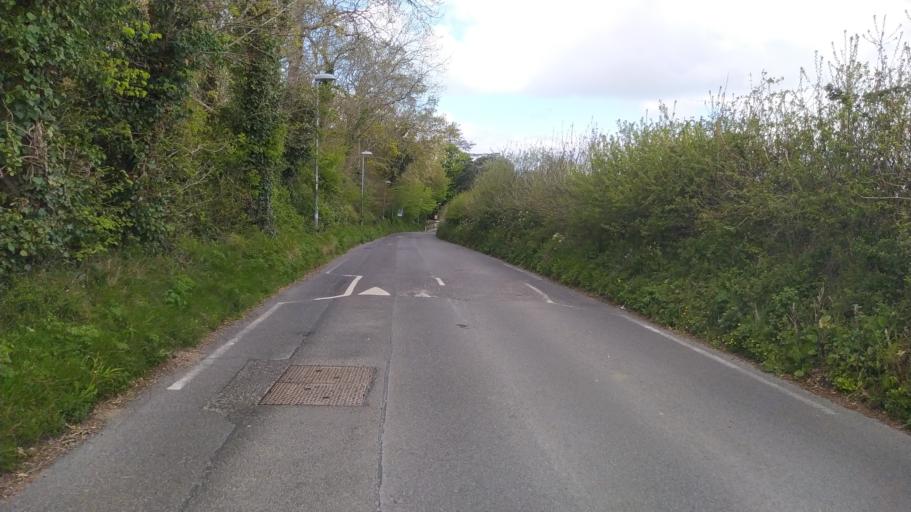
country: GB
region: England
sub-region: Dorset
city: Weymouth
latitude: 50.6432
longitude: -2.4742
